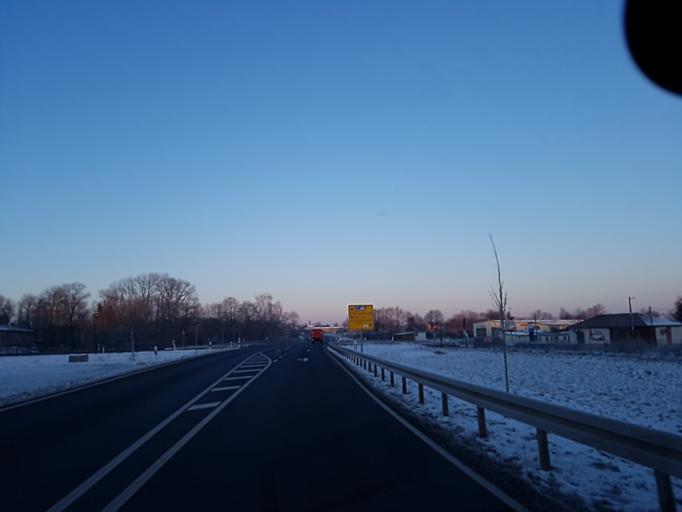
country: DE
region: Saxony
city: Mugeln
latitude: 51.2349
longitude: 13.0701
